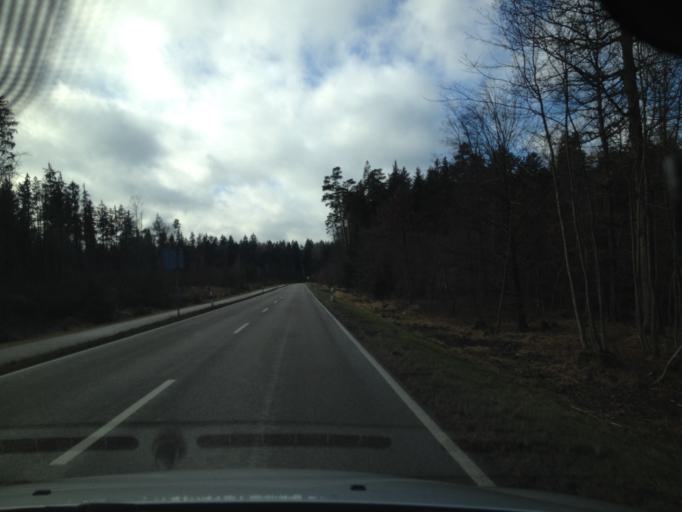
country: DE
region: Bavaria
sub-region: Swabia
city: Wehringen
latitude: 48.2619
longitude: 10.7733
